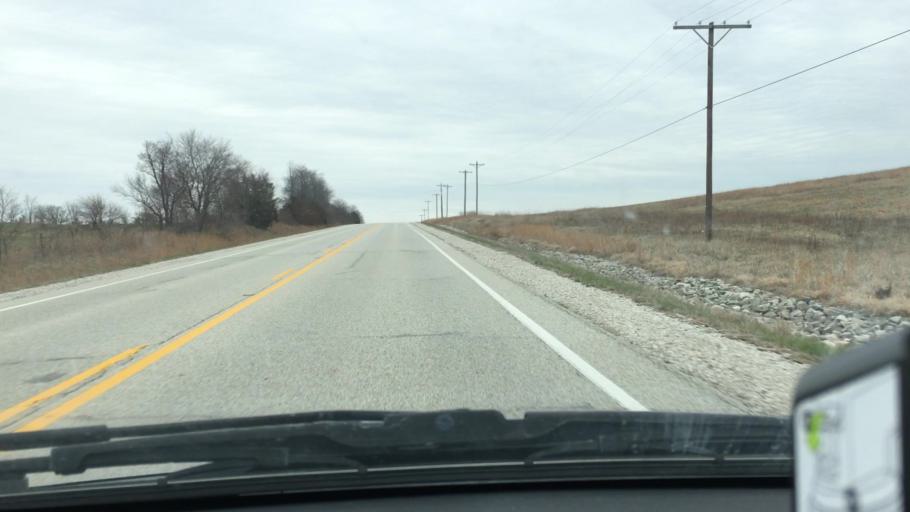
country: US
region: Indiana
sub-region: Greene County
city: Bloomfield
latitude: 39.0121
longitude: -87.0163
